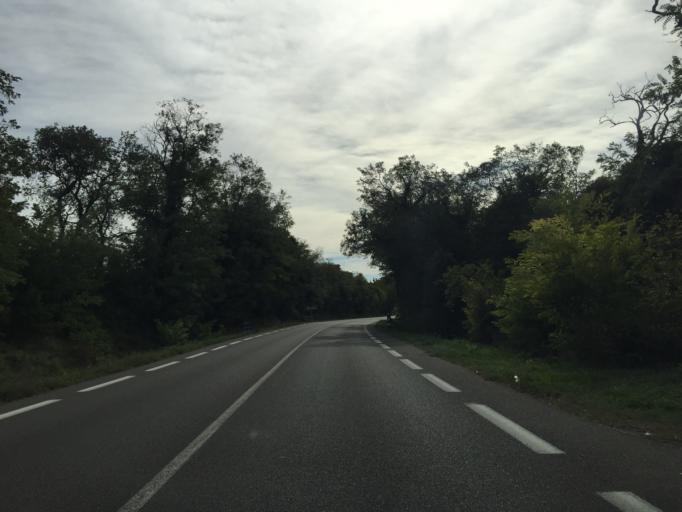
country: FR
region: Provence-Alpes-Cote d'Azur
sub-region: Departement du Vaucluse
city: Bollene
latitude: 44.2705
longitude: 4.7429
